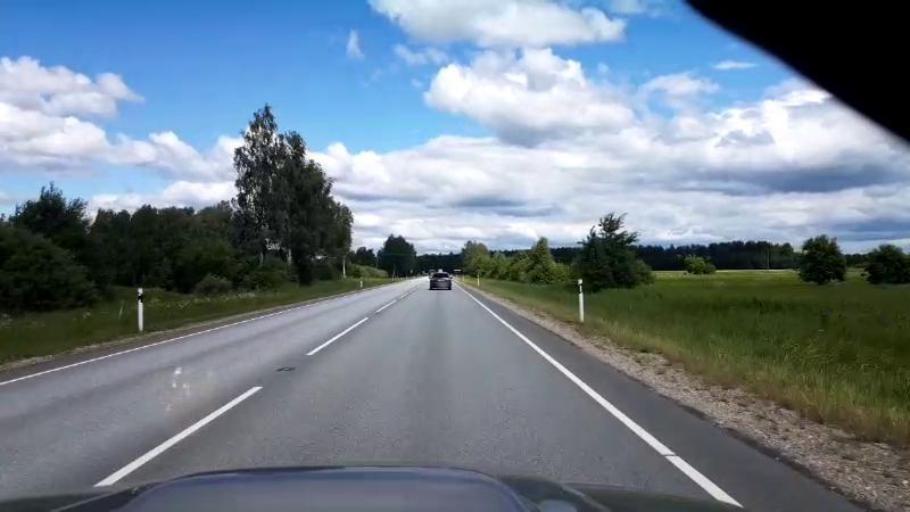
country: EE
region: Paernumaa
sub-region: Sauga vald
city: Sauga
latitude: 58.4532
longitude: 24.5076
